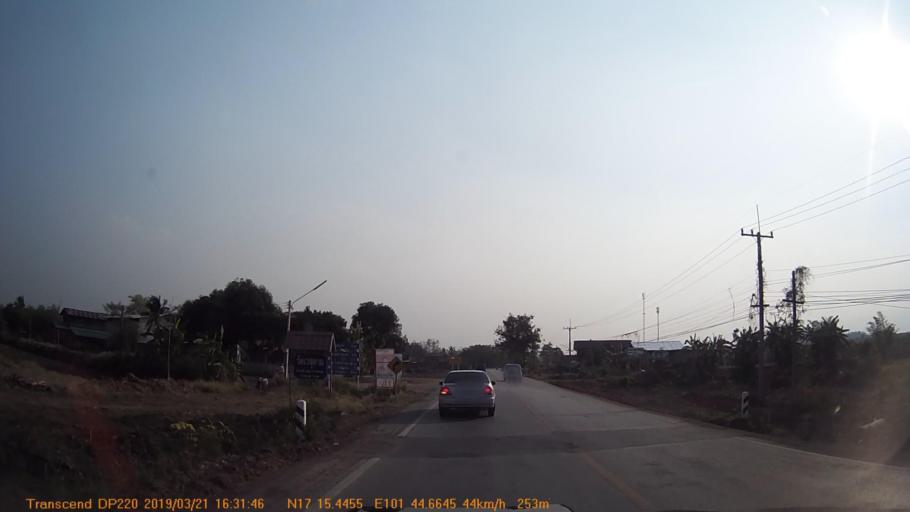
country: TH
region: Loei
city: Wang Saphung
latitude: 17.2572
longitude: 101.7443
